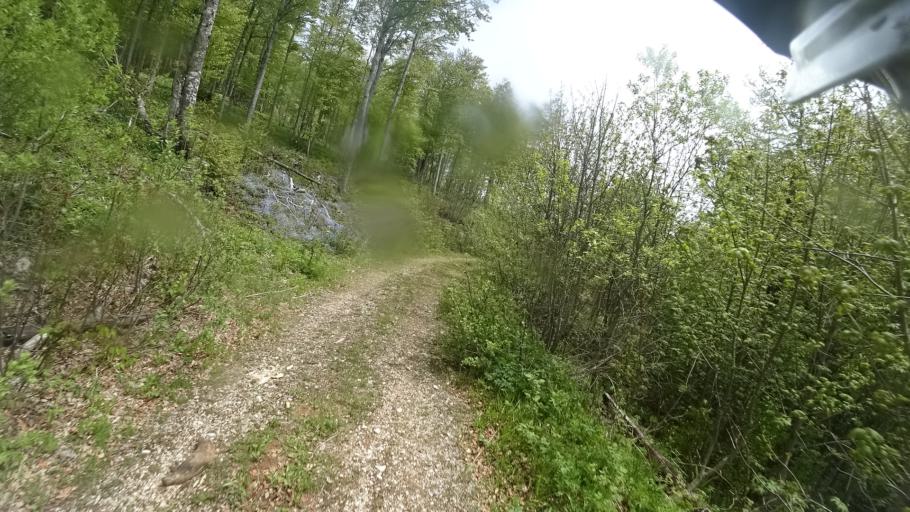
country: BA
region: Federation of Bosnia and Herzegovina
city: Orasac
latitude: 44.5697
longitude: 15.8746
